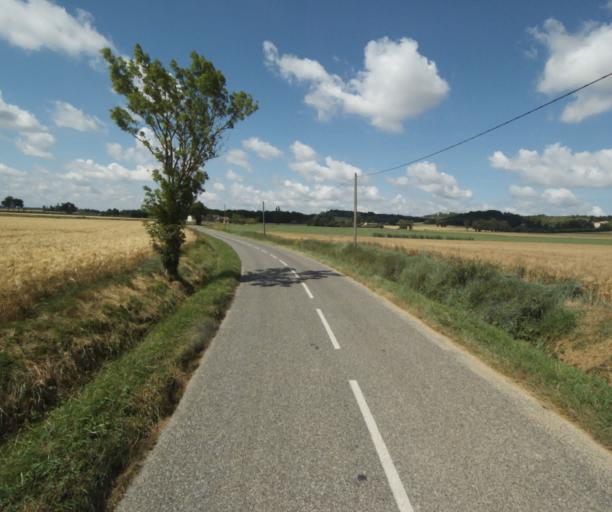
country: FR
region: Midi-Pyrenees
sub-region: Departement de la Haute-Garonne
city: Saint-Felix-Lauragais
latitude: 43.4535
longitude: 1.9202
